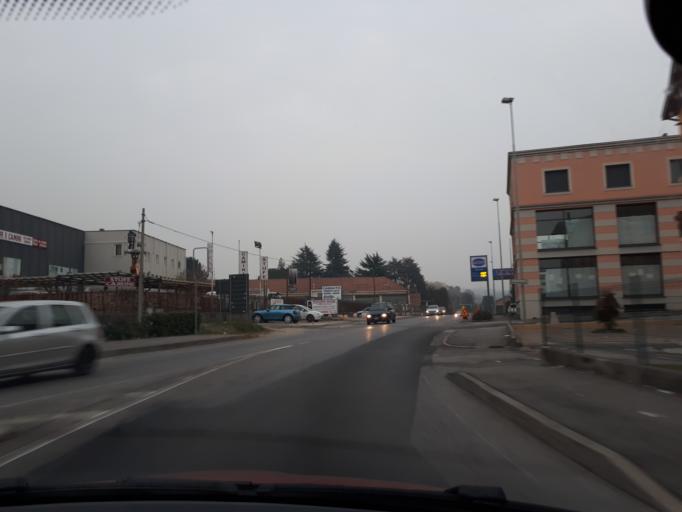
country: IT
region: Lombardy
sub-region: Provincia di Lecco
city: Nibionno
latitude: 45.7482
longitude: 9.2728
